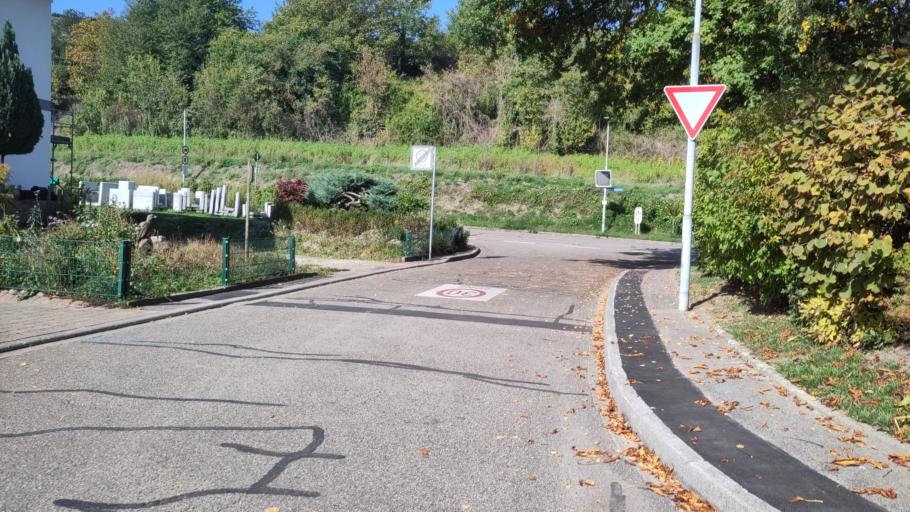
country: DE
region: Baden-Wuerttemberg
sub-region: Freiburg Region
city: Bahlingen
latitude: 48.1185
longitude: 7.7279
